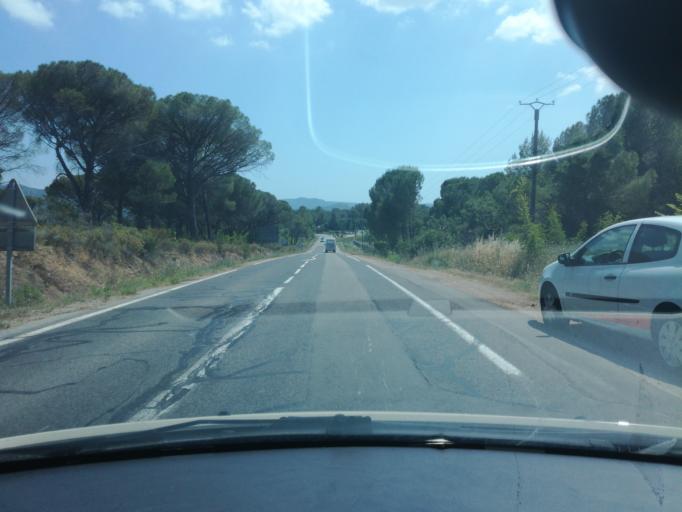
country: FR
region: Provence-Alpes-Cote d'Azur
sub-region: Departement du Var
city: Le Muy
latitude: 43.4922
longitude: 6.5653
